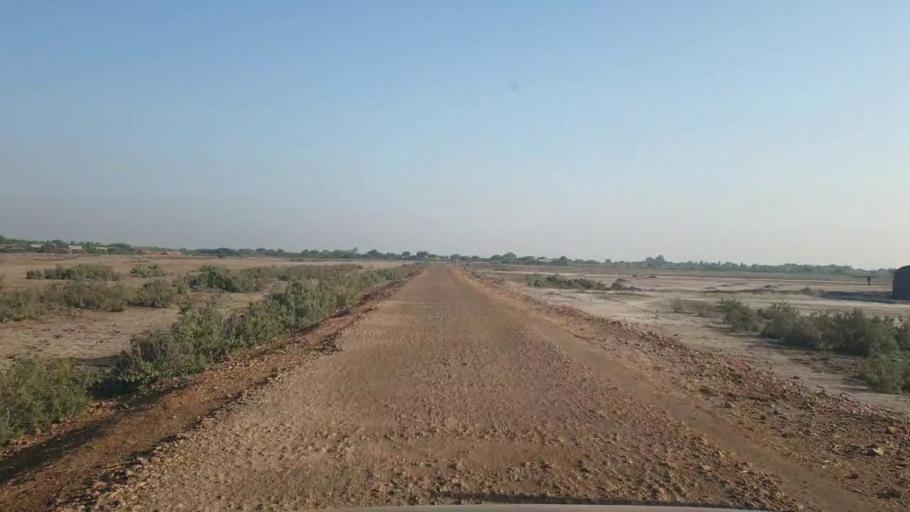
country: PK
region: Sindh
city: Badin
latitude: 24.7262
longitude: 68.8647
